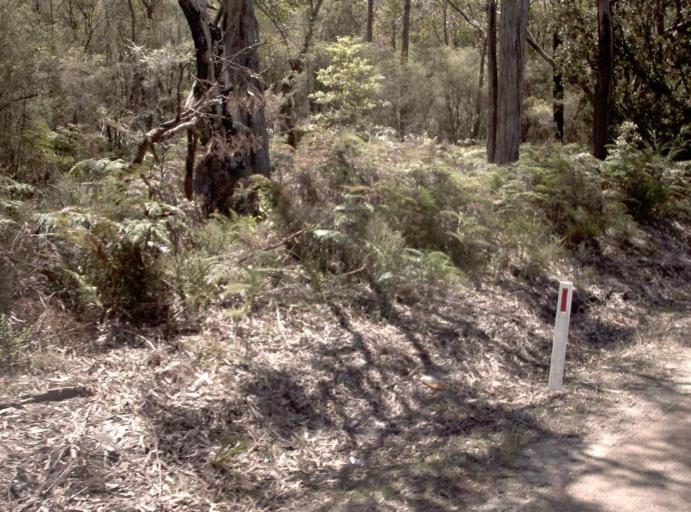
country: AU
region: Victoria
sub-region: East Gippsland
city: Lakes Entrance
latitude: -37.6601
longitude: 148.8027
